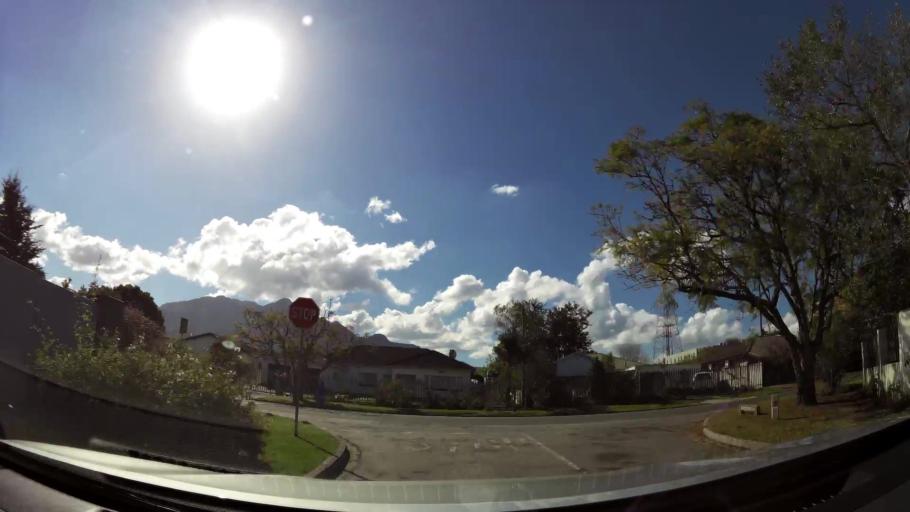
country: ZA
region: Western Cape
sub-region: Eden District Municipality
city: George
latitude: -33.9610
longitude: 22.4521
